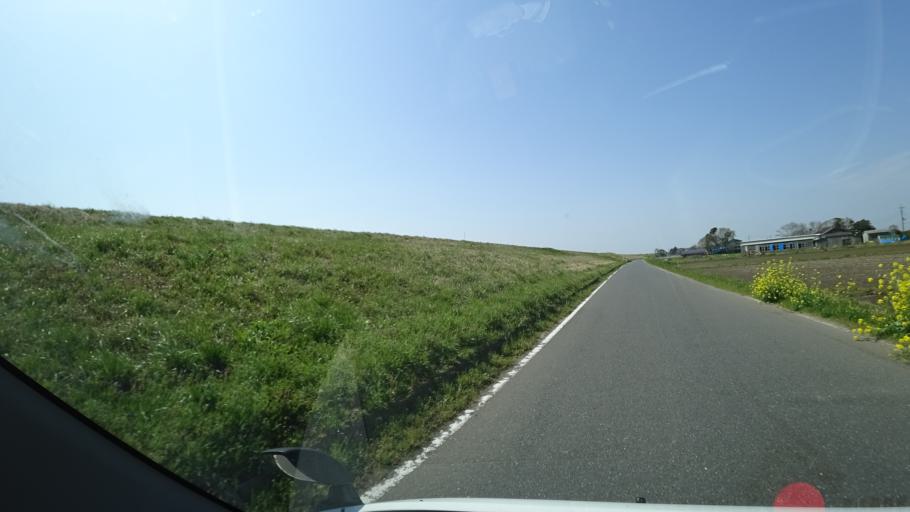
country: JP
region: Ibaraki
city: Edosaki
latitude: 35.8708
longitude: 140.3259
